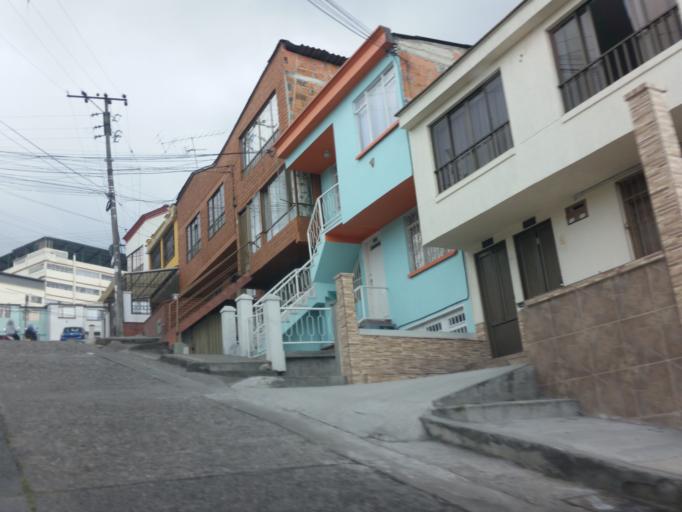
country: CO
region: Caldas
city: Manizales
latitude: 5.0598
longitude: -75.5019
